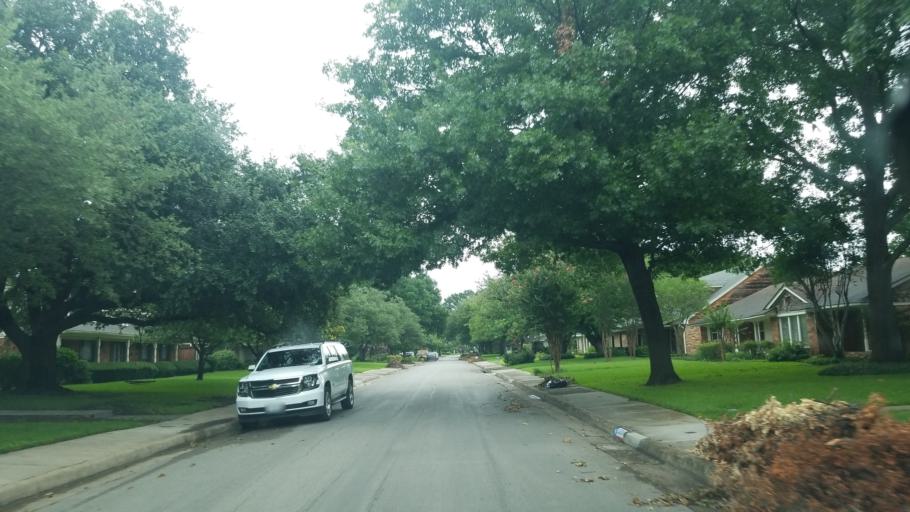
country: US
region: Texas
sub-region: Dallas County
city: Farmers Branch
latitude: 32.8922
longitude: -96.8688
